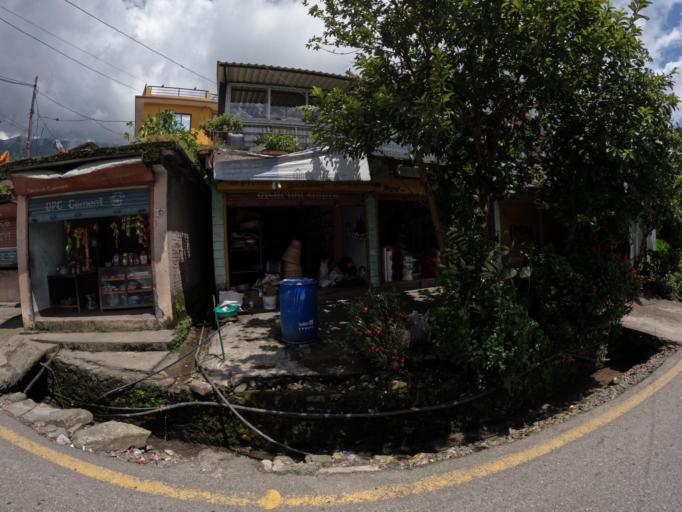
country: NP
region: Central Region
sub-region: Bagmati Zone
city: Kathmandu
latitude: 27.7925
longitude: 85.3300
